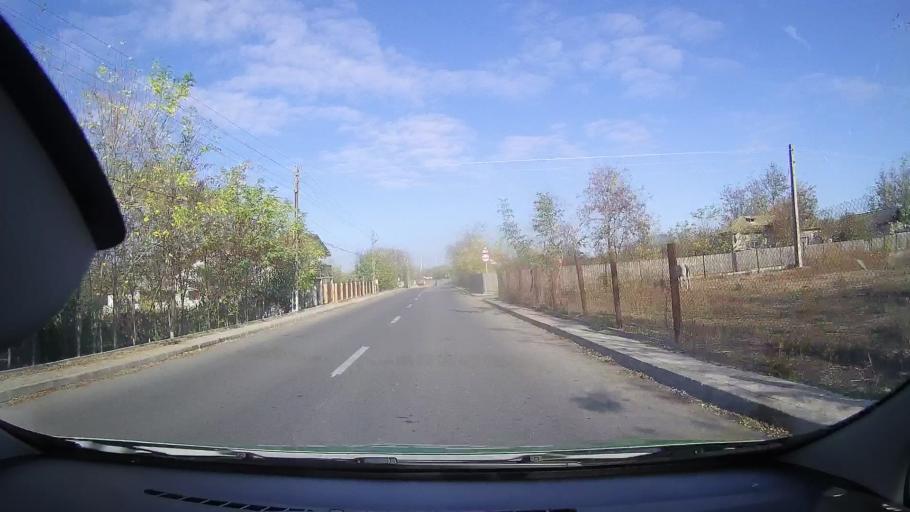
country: RO
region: Tulcea
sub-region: Comuna Valea Nucarilor
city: Valea Nucarilor
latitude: 45.0382
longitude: 28.9402
